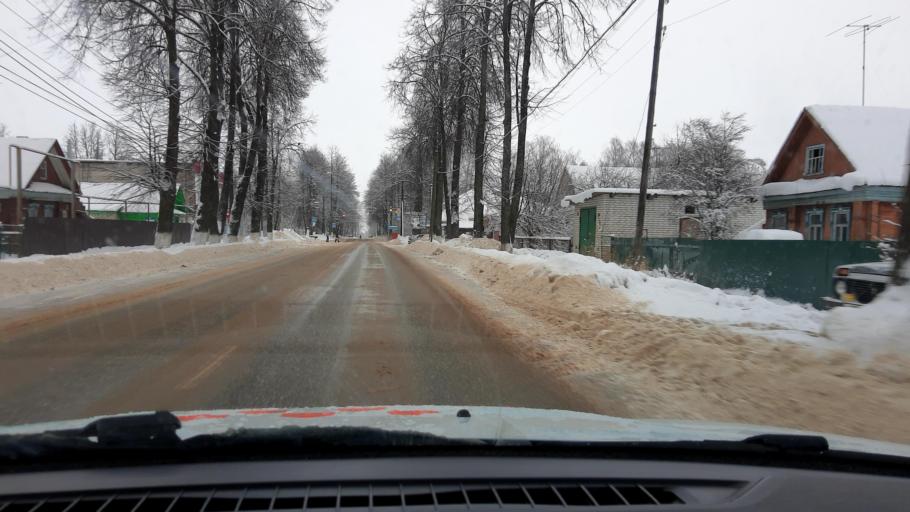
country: RU
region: Nizjnij Novgorod
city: Chkalovsk
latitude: 56.7646
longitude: 43.2487
